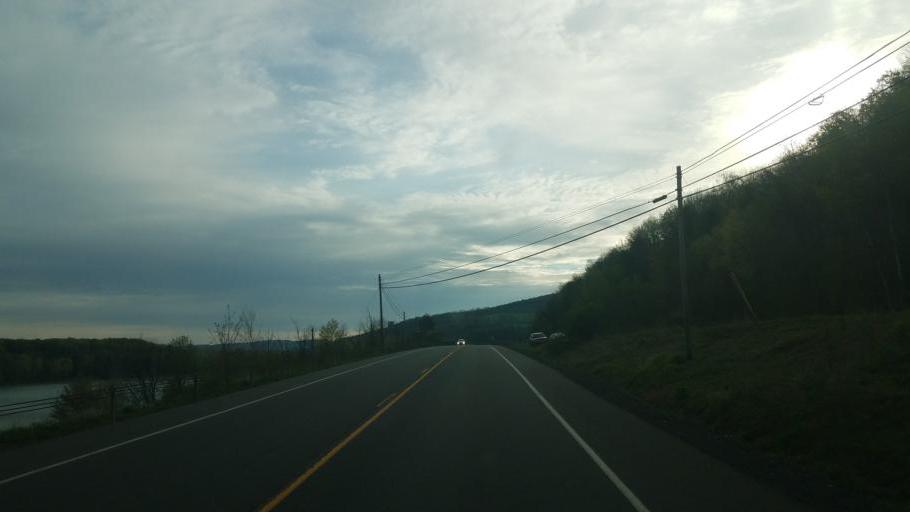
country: US
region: New York
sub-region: Steuben County
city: Hornell
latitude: 42.3416
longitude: -77.7155
